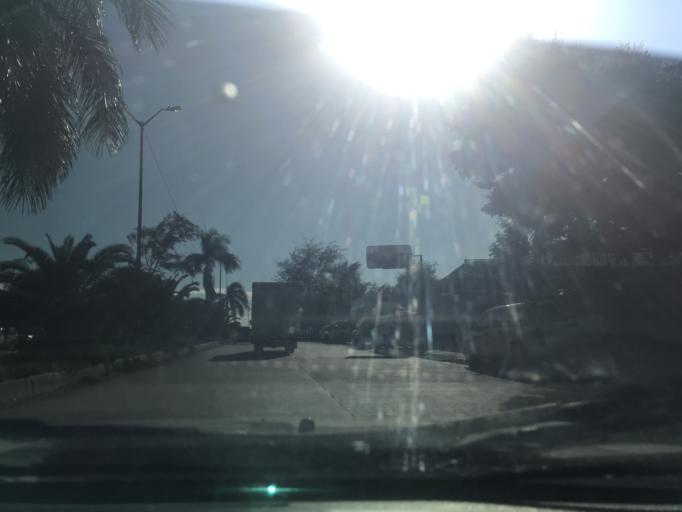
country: DO
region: Santiago
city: Santiago de los Caballeros
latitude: 19.4257
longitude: -70.6761
